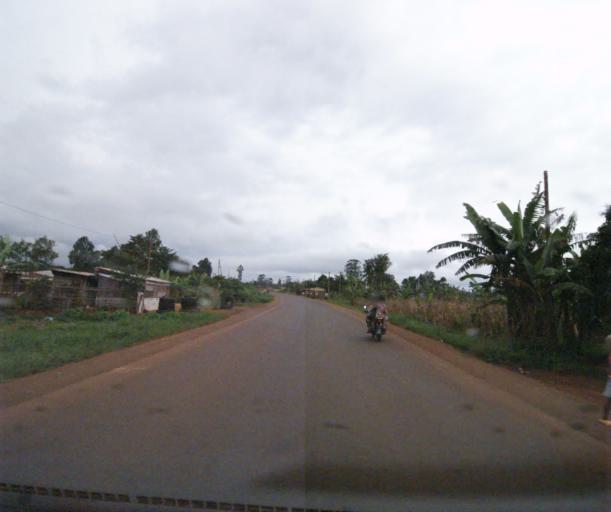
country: CM
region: West
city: Dschang
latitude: 5.4918
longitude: 10.1650
